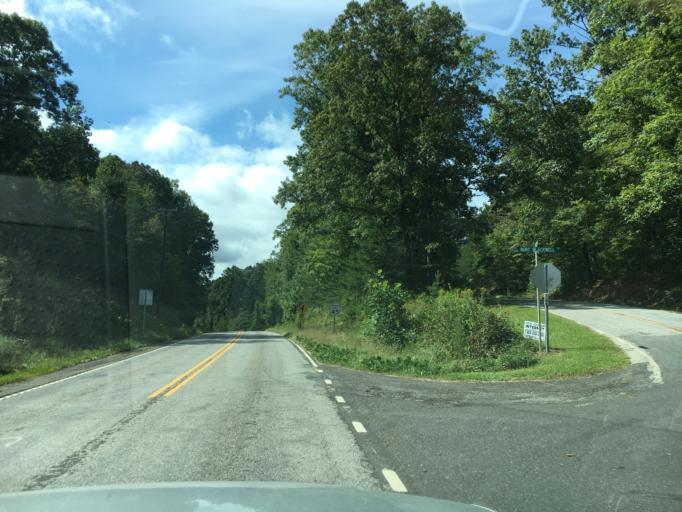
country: US
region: North Carolina
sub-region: Polk County
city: Columbus
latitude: 35.3186
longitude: -82.1762
